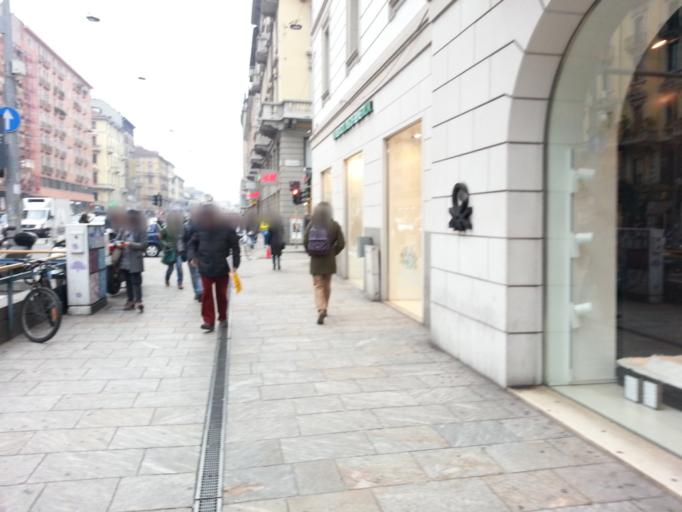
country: IT
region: Lombardy
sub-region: Citta metropolitana di Milano
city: Milano
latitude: 45.4778
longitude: 9.2088
